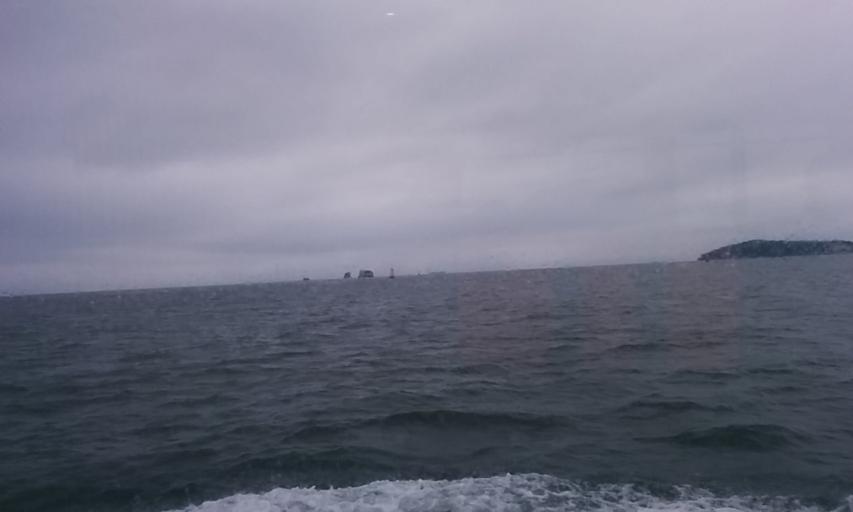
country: JP
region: Miyagi
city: Matsushima
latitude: 38.3230
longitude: 141.0999
